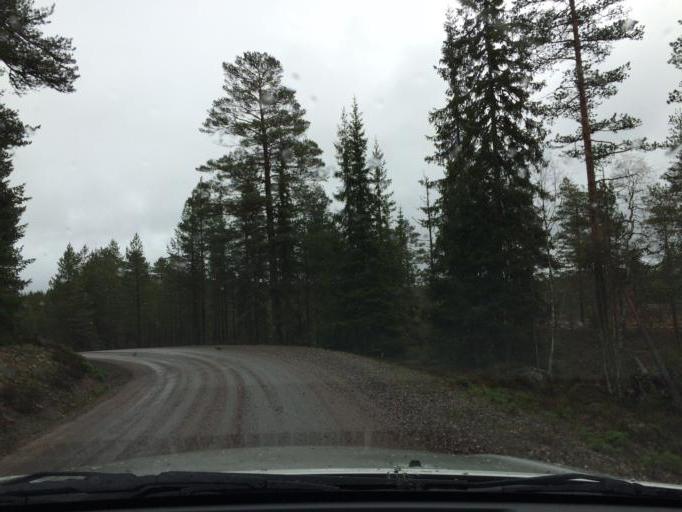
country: SE
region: OErebro
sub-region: Hallefors Kommun
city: Haellefors
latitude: 60.0236
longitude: 14.5610
